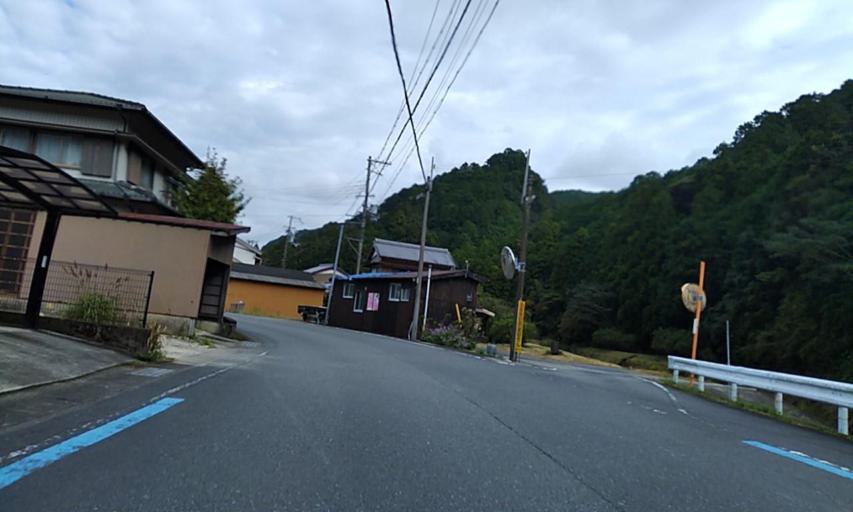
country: JP
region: Wakayama
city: Shingu
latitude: 33.5376
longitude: 135.8193
